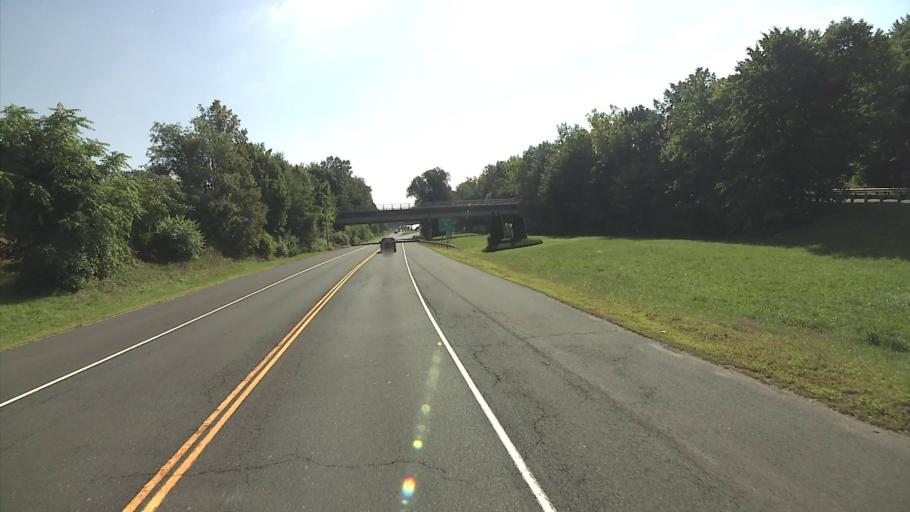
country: US
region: Connecticut
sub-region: Hartford County
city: Thompsonville
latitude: 41.9904
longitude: -72.5992
